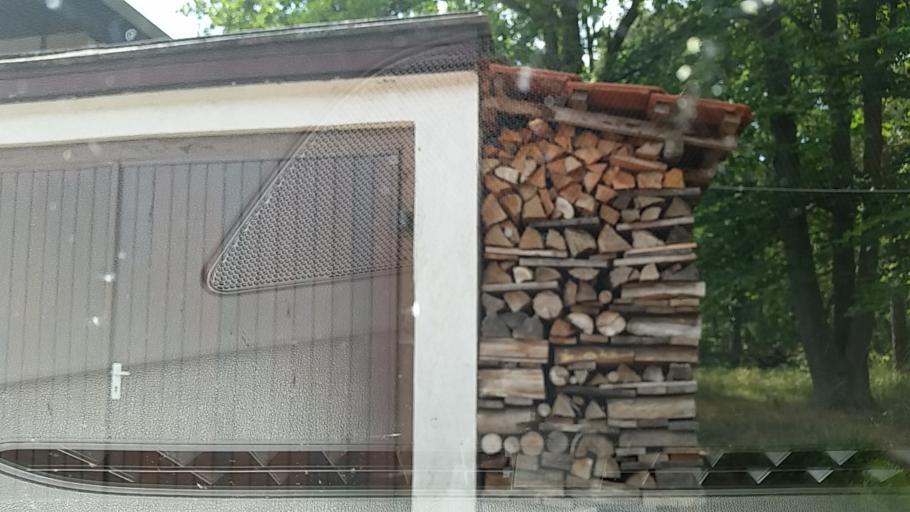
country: DE
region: Lower Saxony
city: Edemissen
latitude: 52.3893
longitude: 10.3199
